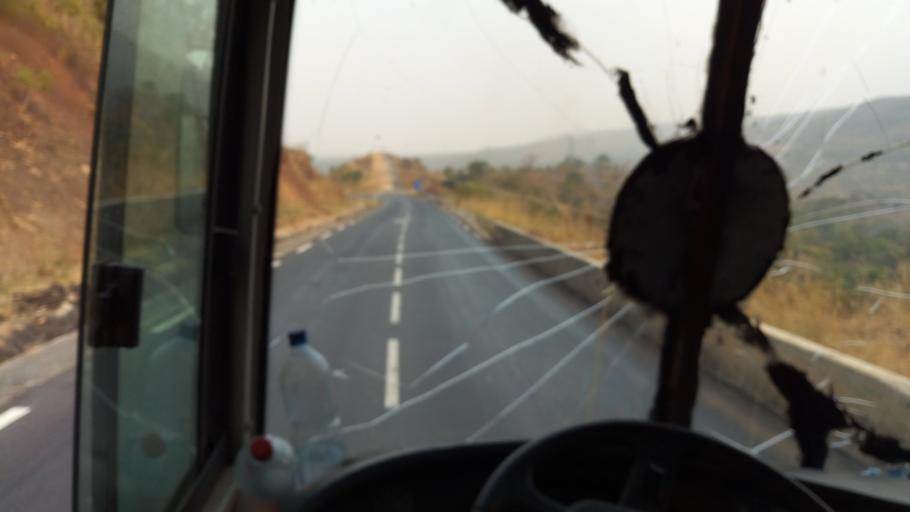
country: TG
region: Kara
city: Bafilo
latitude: 9.3478
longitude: 1.2681
